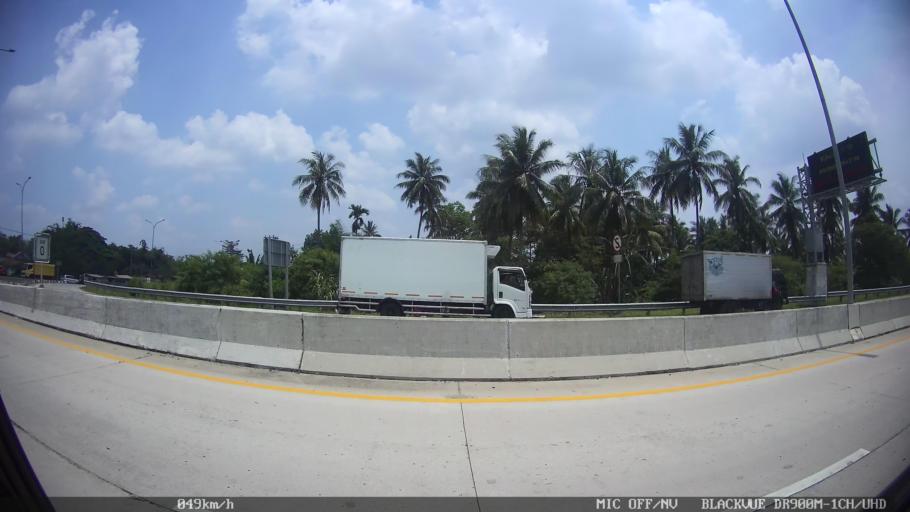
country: ID
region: Lampung
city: Natar
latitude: -5.2818
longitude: 105.1907
